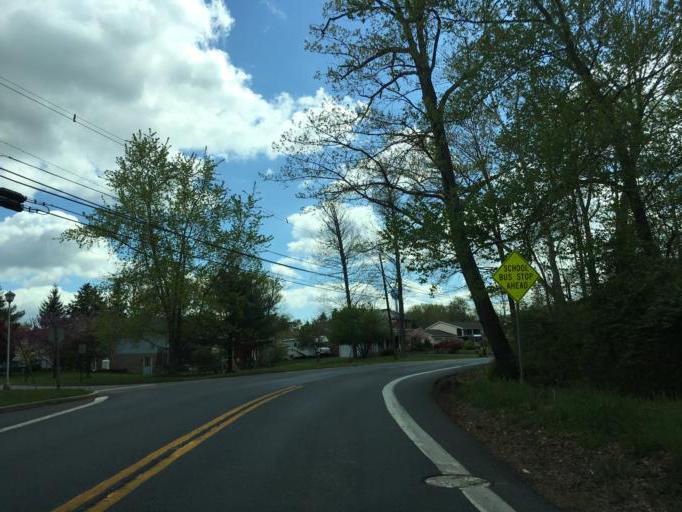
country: US
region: Maryland
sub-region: Frederick County
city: Thurmont
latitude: 39.6218
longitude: -77.4218
